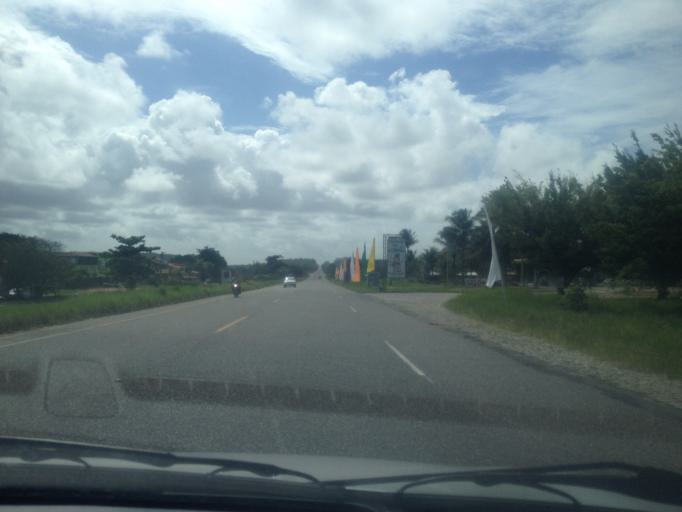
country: BR
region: Bahia
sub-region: Entre Rios
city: Entre Rios
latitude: -12.3028
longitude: -37.9010
